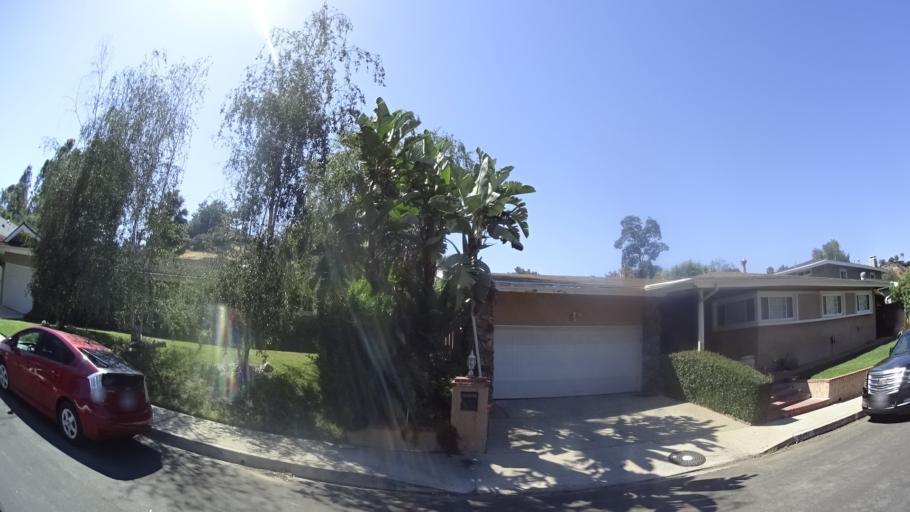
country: US
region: California
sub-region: Los Angeles County
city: Sherman Oaks
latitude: 34.1358
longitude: -118.4851
